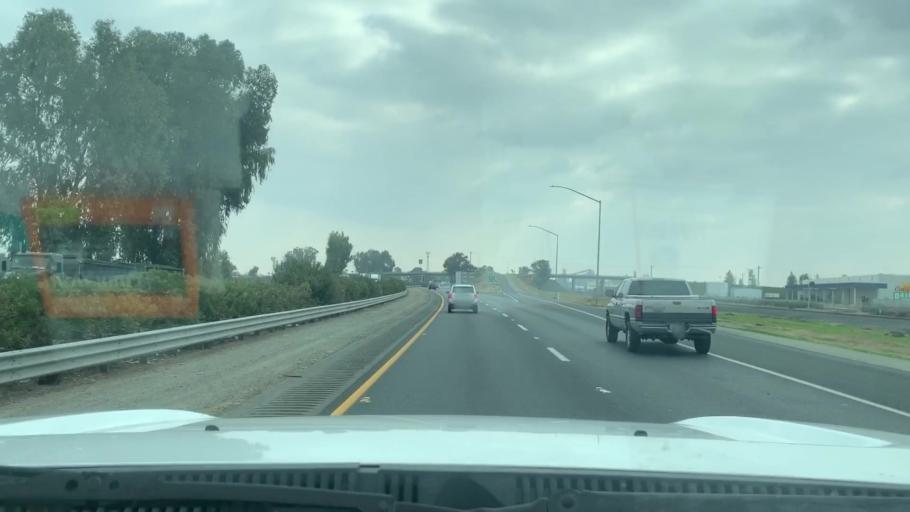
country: US
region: California
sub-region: Tulare County
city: Pixley
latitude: 36.0116
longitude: -119.3034
